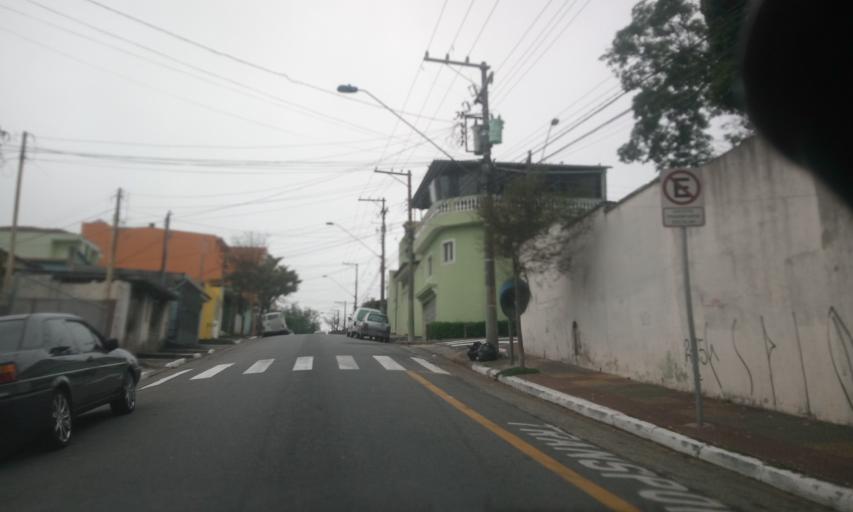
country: BR
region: Sao Paulo
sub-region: Sao Caetano Do Sul
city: Sao Caetano do Sul
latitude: -23.6424
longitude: -46.5688
